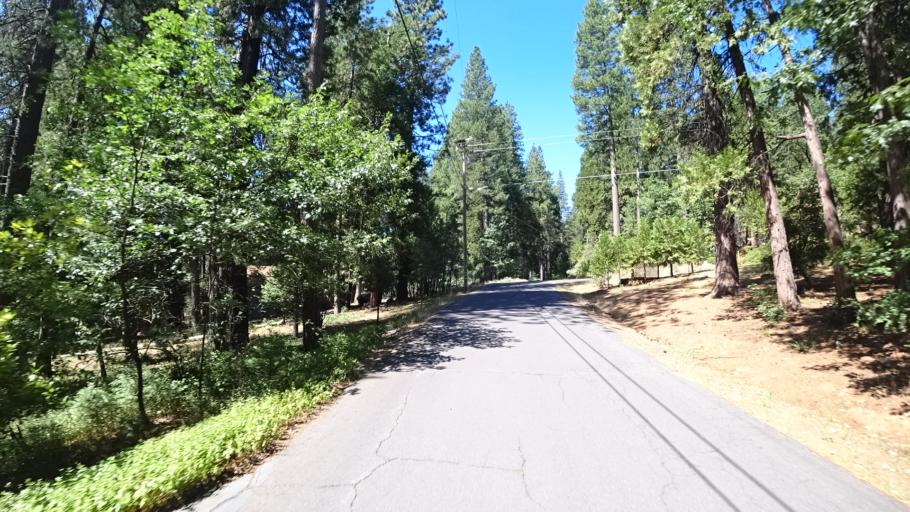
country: US
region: California
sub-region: Calaveras County
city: Arnold
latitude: 38.2398
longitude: -120.3684
